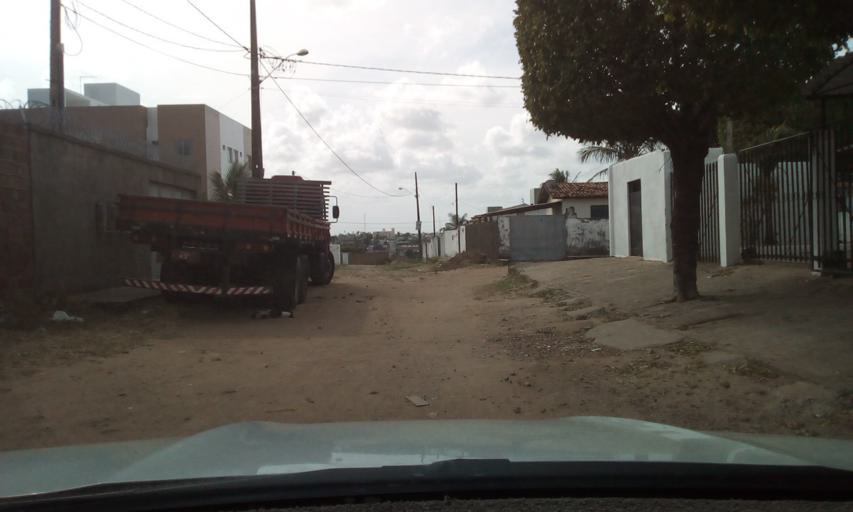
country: BR
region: Paraiba
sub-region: Joao Pessoa
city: Joao Pessoa
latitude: -7.1644
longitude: -34.8831
